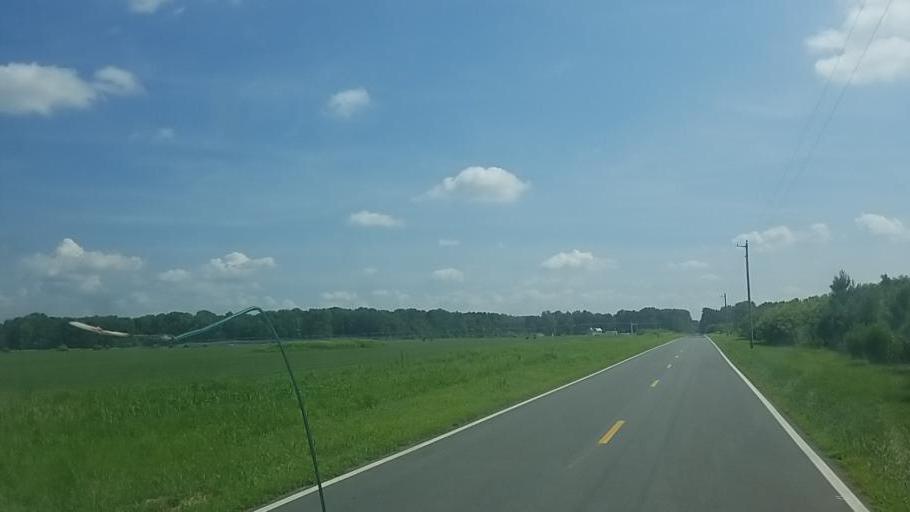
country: US
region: Maryland
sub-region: Wicomico County
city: Hebron
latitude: 38.4307
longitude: -75.6979
